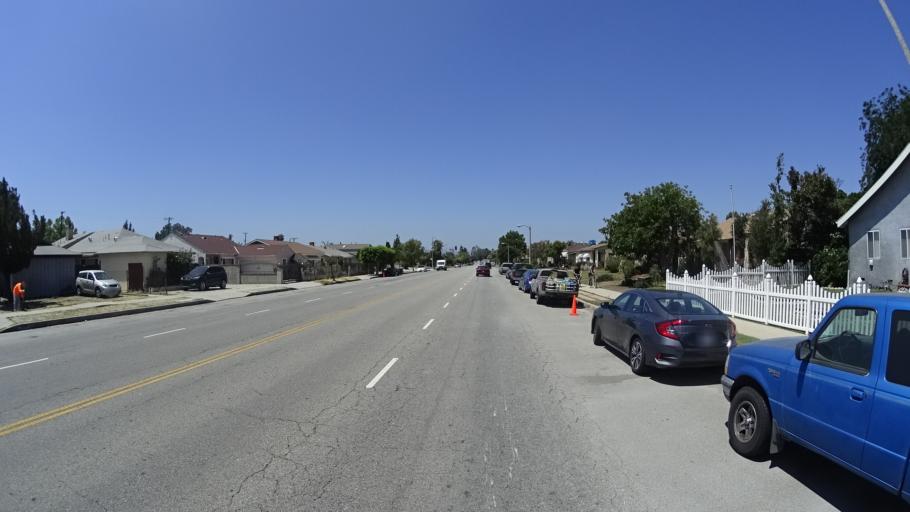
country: US
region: California
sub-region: Los Angeles County
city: Van Nuys
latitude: 34.2298
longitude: -118.4281
